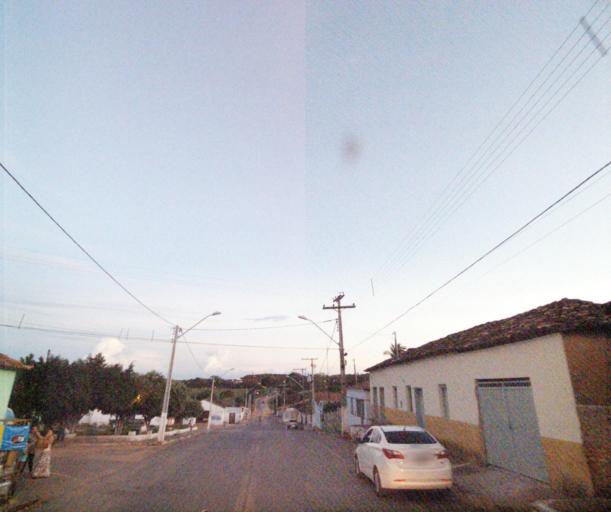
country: BR
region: Bahia
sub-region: Sao Felix Do Coribe
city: Santa Maria da Vitoria
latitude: -13.8310
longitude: -44.4544
